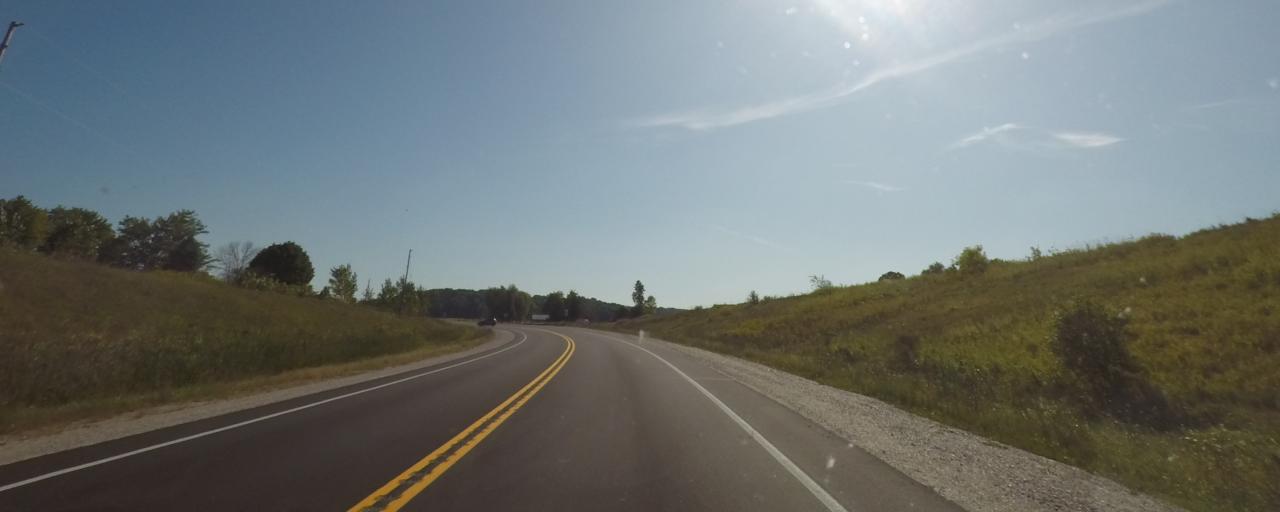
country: US
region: Wisconsin
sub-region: Jefferson County
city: Ixonia
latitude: 43.0099
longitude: -88.6473
